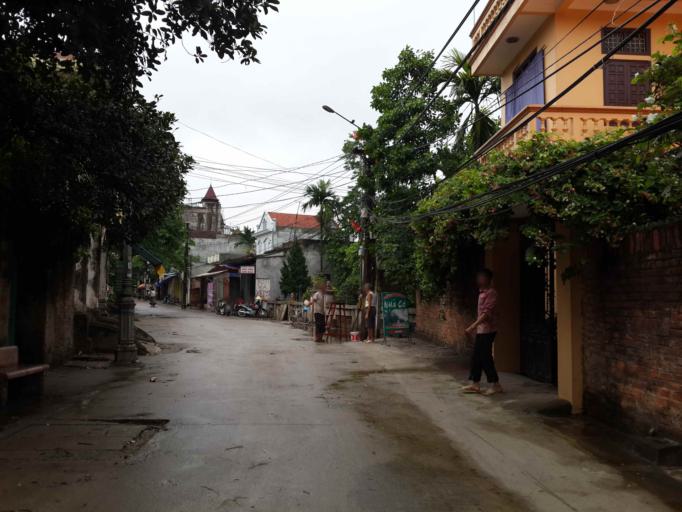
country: VN
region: Ha Noi
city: Son Tay
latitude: 21.1604
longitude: 105.4692
